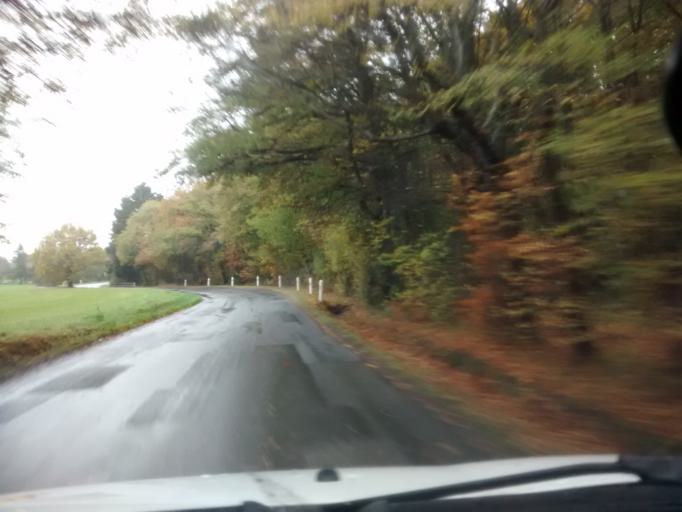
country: FR
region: Brittany
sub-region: Departement d'Ille-et-Vilaine
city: Chantepie
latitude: 48.0745
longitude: -1.6050
